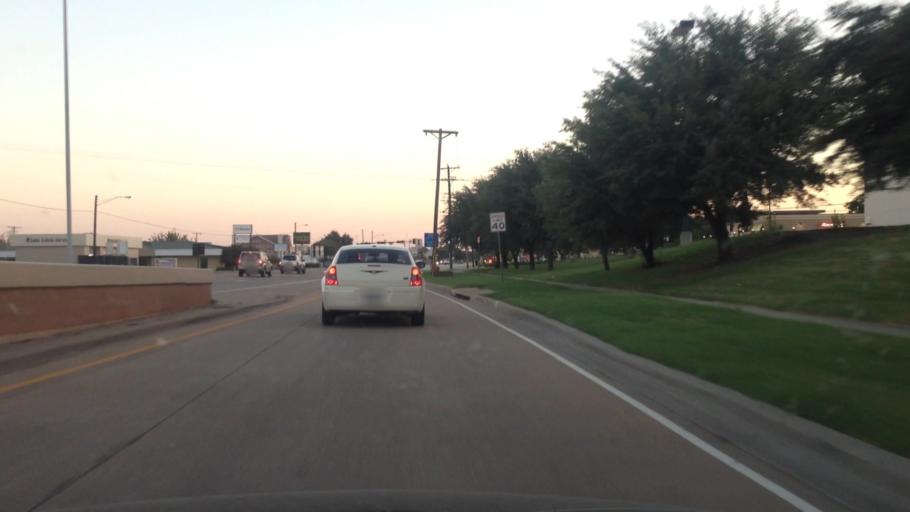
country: US
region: Texas
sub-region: Tarrant County
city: North Richland Hills
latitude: 32.8366
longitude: -97.2140
